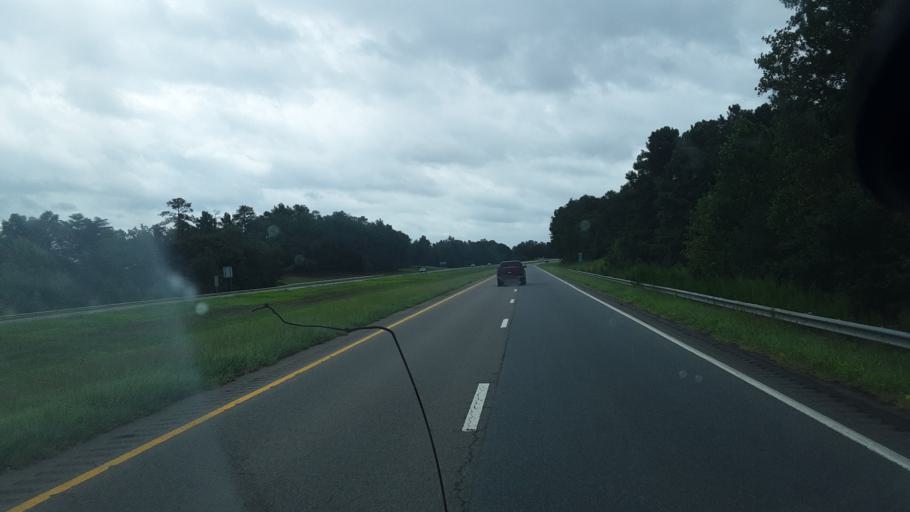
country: US
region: North Carolina
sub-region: Montgomery County
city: Biscoe
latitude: 35.2660
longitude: -79.7273
